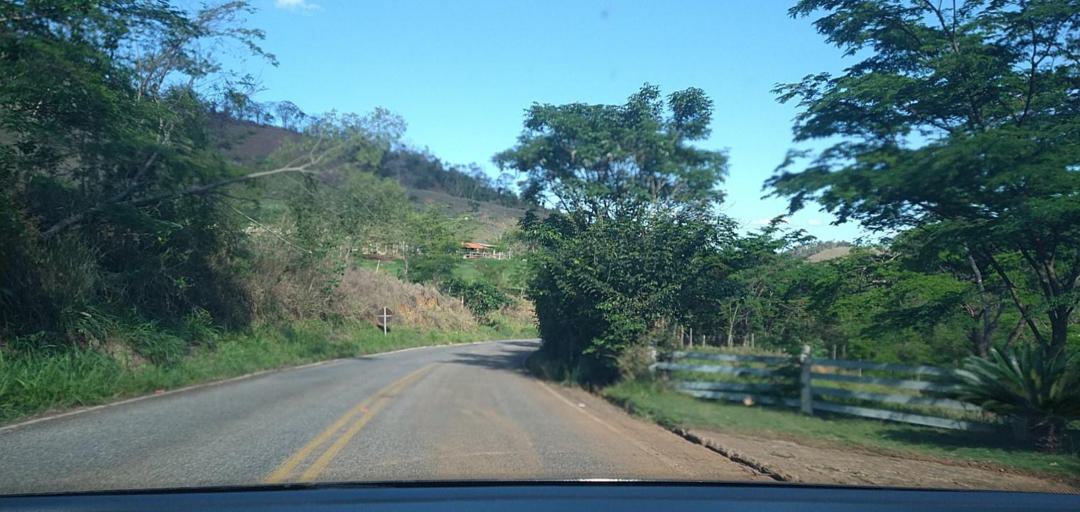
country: BR
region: Minas Gerais
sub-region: Alvinopolis
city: Alvinopolis
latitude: -20.1945
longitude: -42.9329
